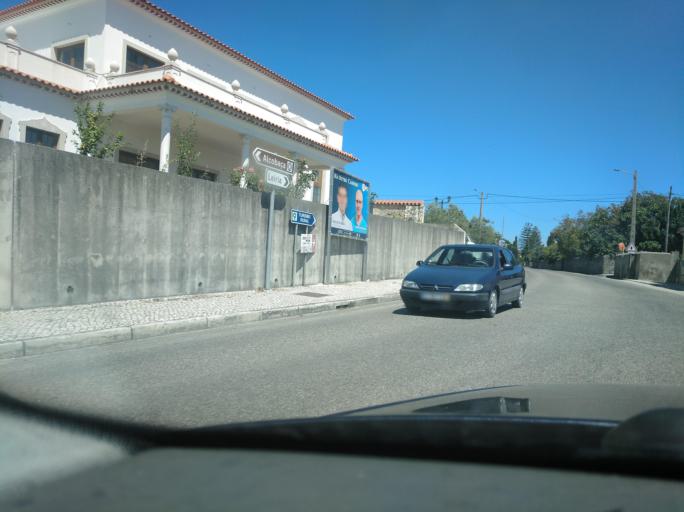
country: PT
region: Leiria
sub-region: Alcobaca
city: Aljubarrota
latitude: 39.5664
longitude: -8.9280
